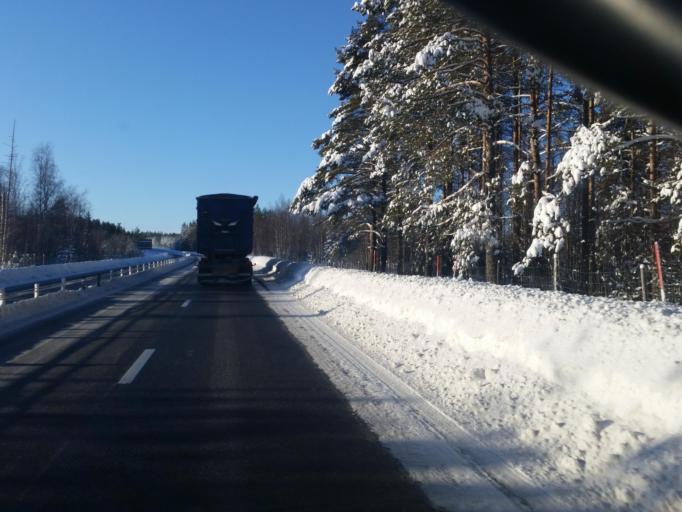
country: SE
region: Norrbotten
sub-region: Pitea Kommun
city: Hortlax
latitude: 65.0979
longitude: 21.4986
